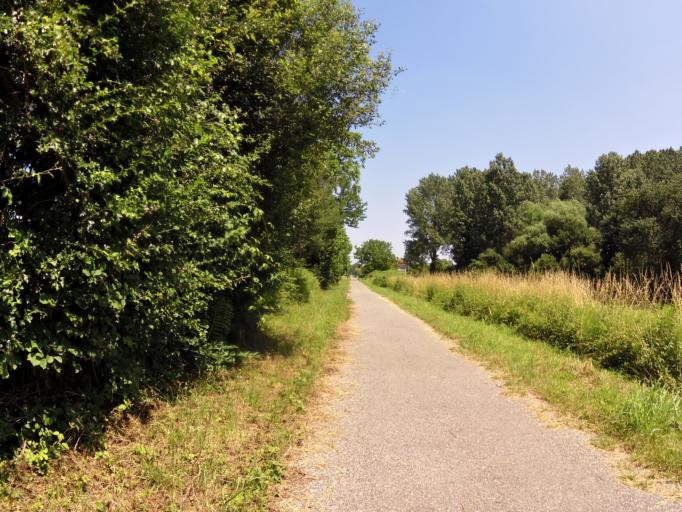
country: FR
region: Aquitaine
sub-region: Departement des Pyrenees-Atlantiques
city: Salies-de-Bearn
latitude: 43.4564
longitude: -0.9903
